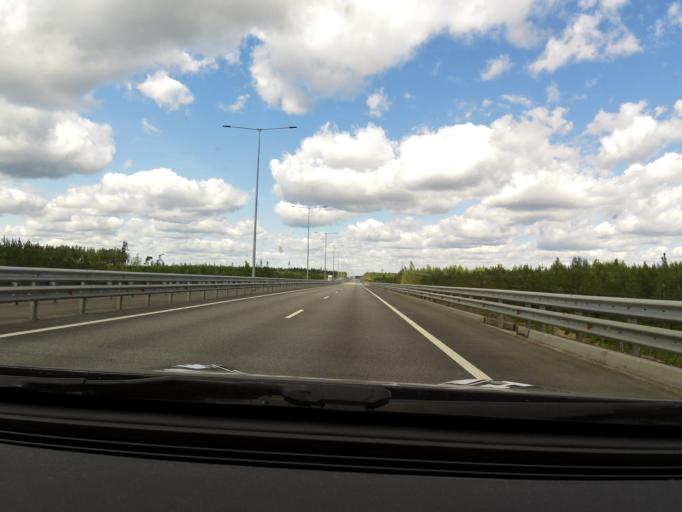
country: RU
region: Tverskaya
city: Vyshniy Volochek
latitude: 57.4355
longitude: 34.4580
